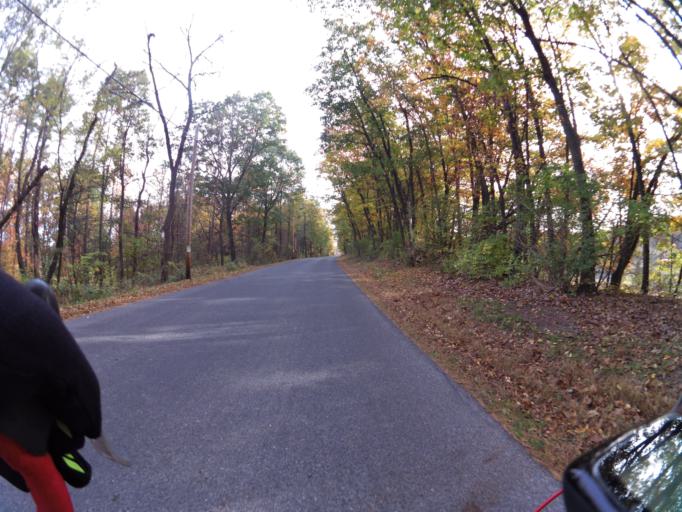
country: US
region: Pennsylvania
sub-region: Union County
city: New Columbia
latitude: 41.0428
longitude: -76.9116
